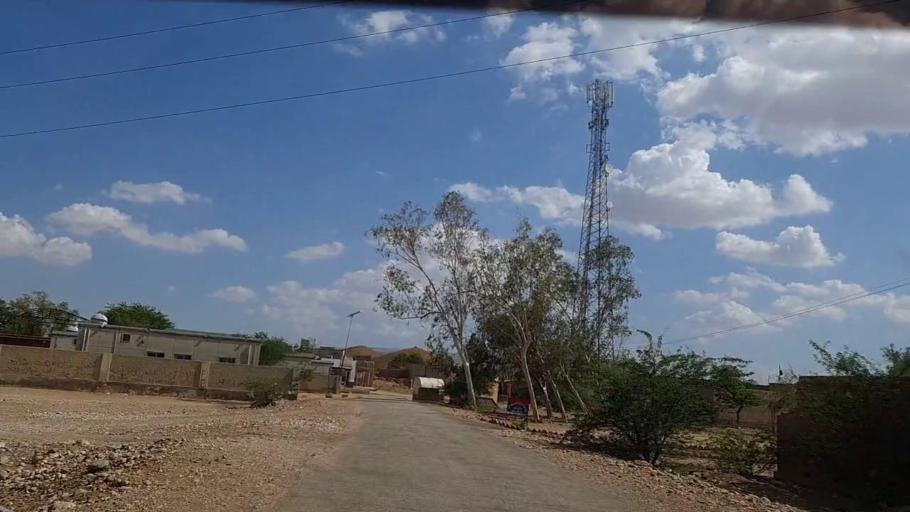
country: PK
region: Sindh
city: Johi
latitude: 26.4977
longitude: 67.4317
